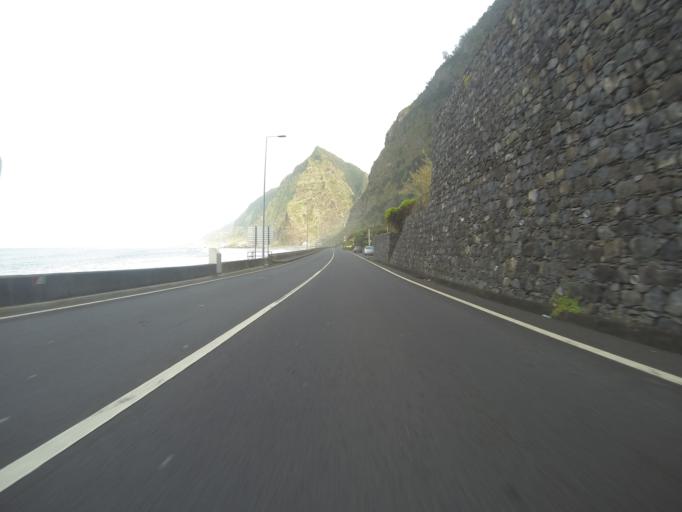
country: PT
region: Madeira
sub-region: Sao Vicente
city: Sao Vicente
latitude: 32.8098
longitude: -17.0629
